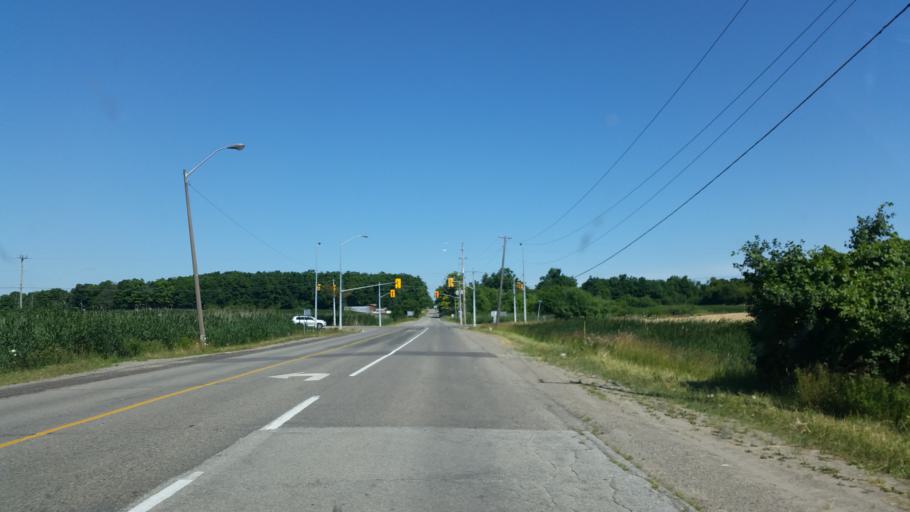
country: CA
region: Ontario
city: Brampton
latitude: 43.7918
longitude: -79.8559
